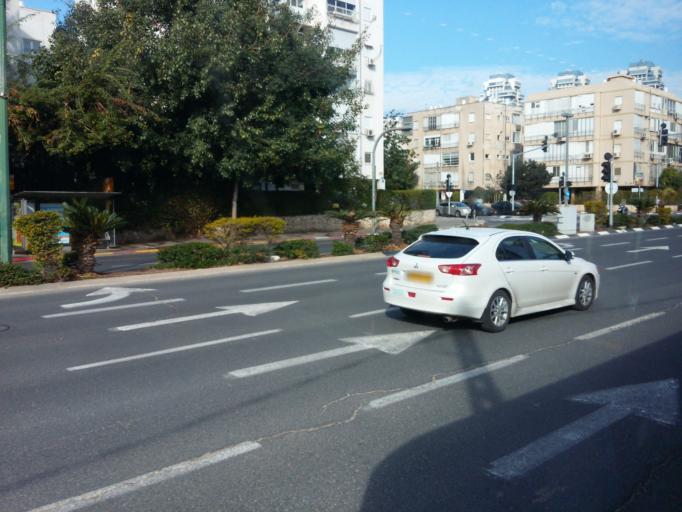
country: IL
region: Tel Aviv
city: Tel Aviv
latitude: 32.0849
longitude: 34.7949
